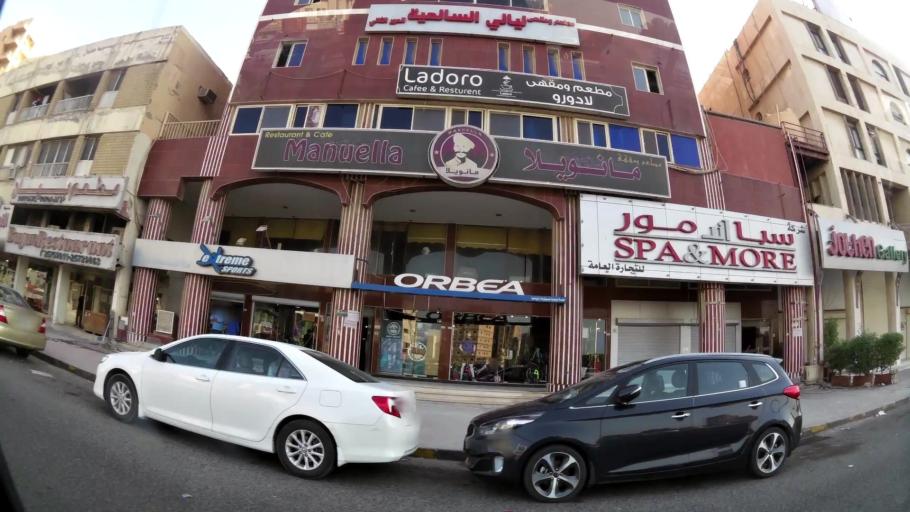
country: KW
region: Muhafazat Hawalli
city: As Salimiyah
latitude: 29.3342
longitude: 48.0665
